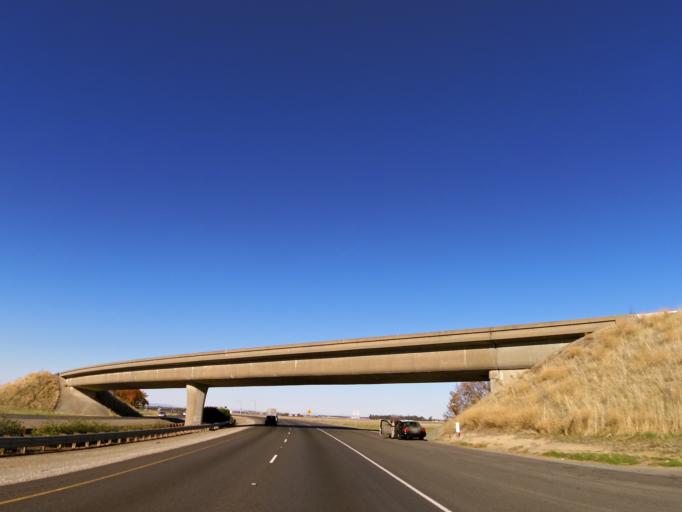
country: US
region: California
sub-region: Yolo County
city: West Sacramento
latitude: 38.6691
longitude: -121.5421
